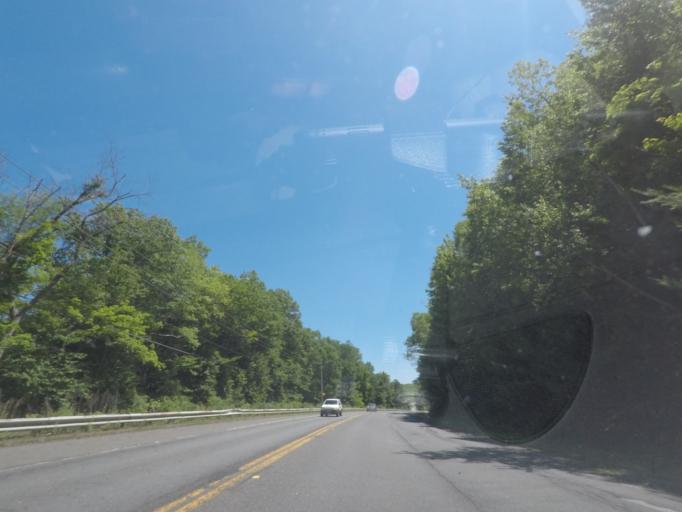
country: US
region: Massachusetts
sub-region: Hampden County
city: Westfield
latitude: 42.1772
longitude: -72.8348
